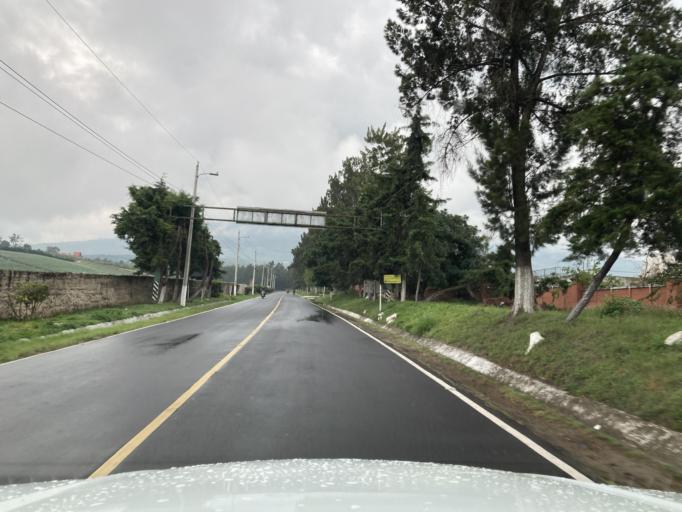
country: GT
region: Sacatepequez
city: San Miguel Duenas
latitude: 14.5208
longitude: -90.7908
